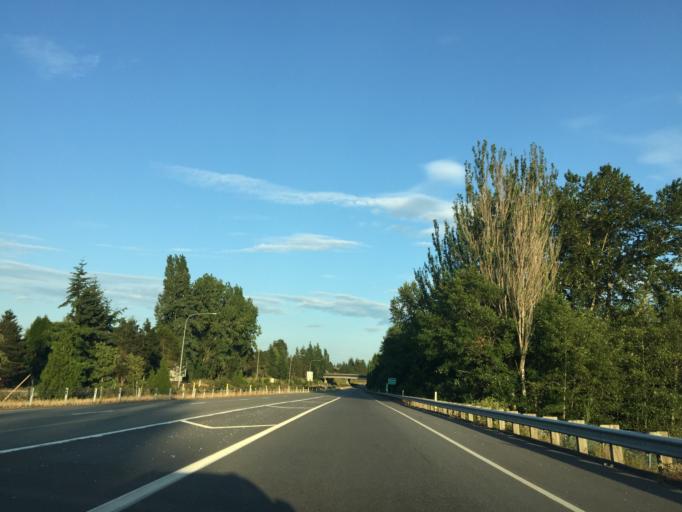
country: US
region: Washington
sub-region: Whatcom County
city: Blaine
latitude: 48.9963
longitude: -122.7500
